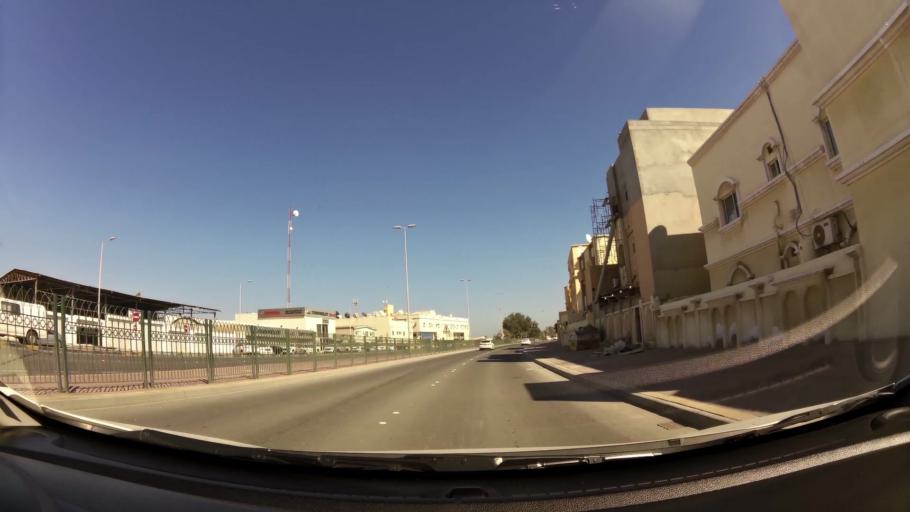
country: BH
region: Muharraq
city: Al Hadd
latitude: 26.2562
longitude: 50.6464
